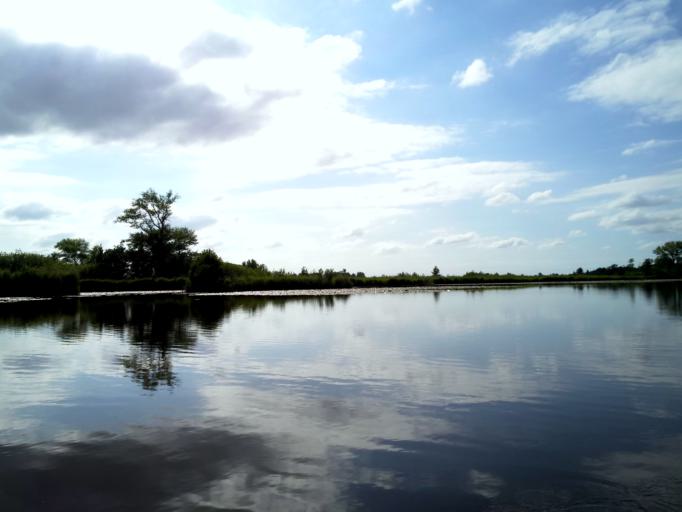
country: NL
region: Friesland
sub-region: Gemeente Boarnsterhim
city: Warten
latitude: 53.1259
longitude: 5.9172
